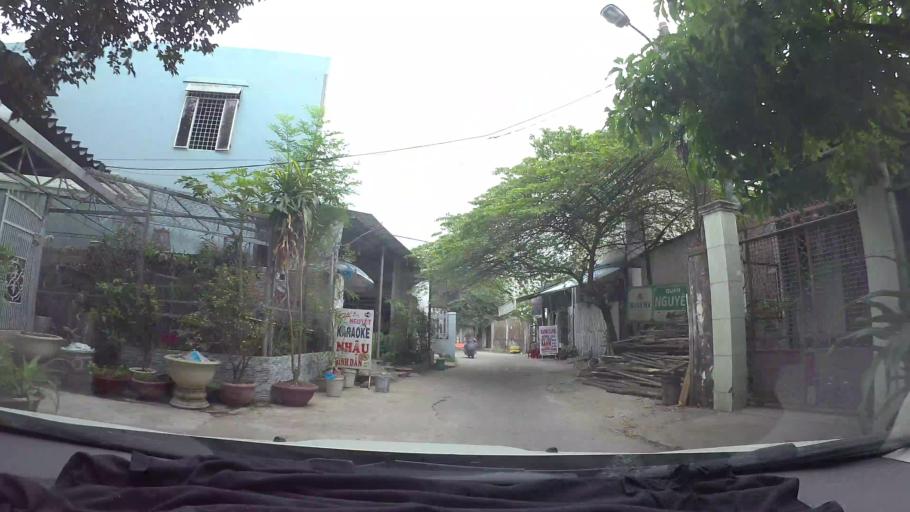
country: VN
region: Da Nang
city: Lien Chieu
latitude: 16.0749
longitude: 108.1474
